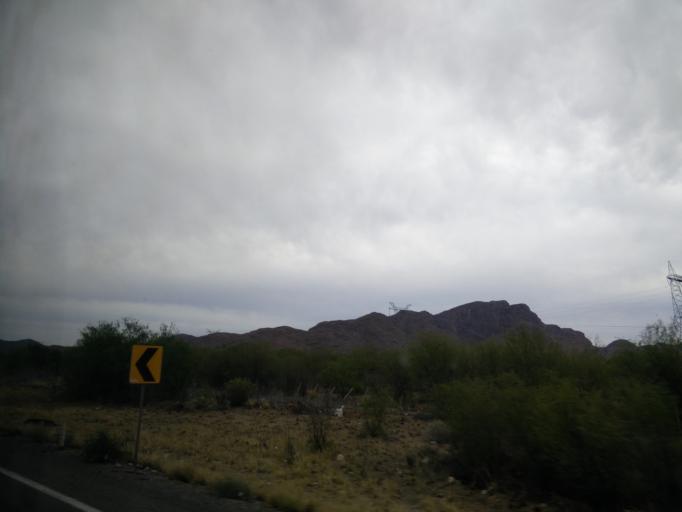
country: MX
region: Sonora
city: Hermosillo
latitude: 28.5889
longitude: -111.0248
